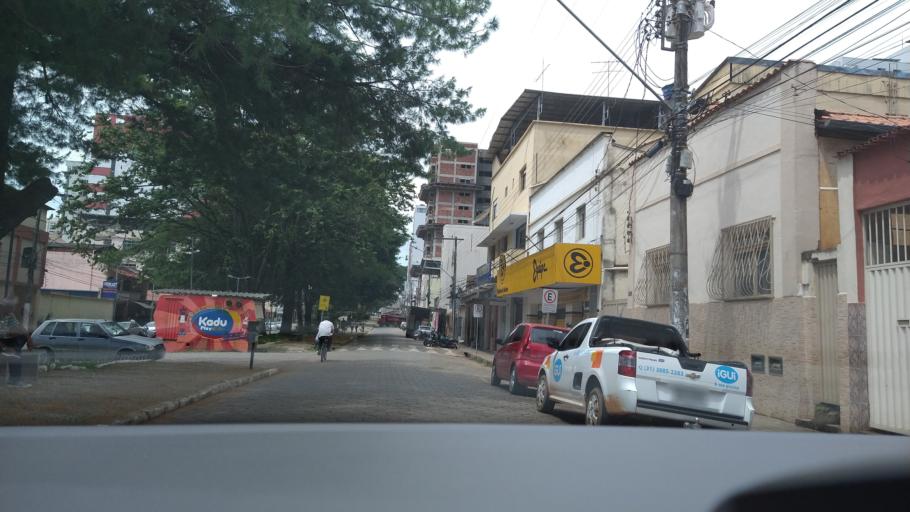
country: BR
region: Minas Gerais
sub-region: Vicosa
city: Vicosa
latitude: -20.7590
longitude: -42.8794
